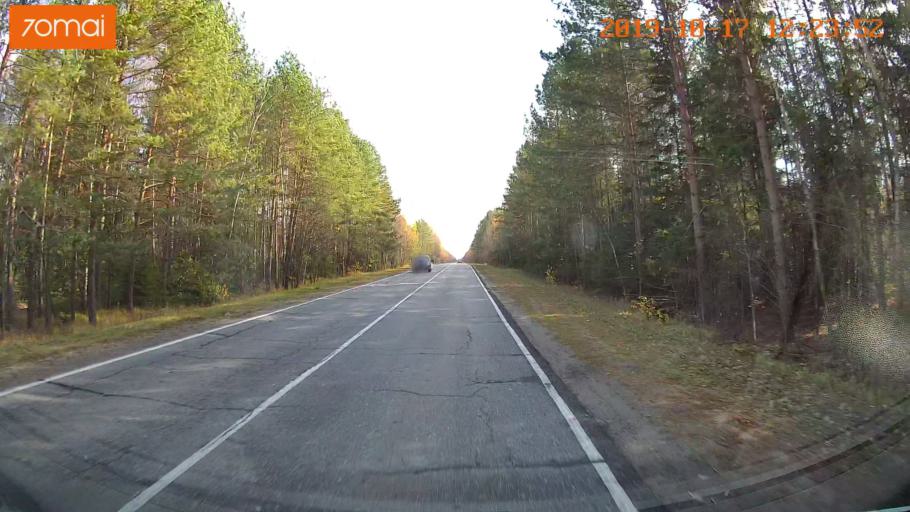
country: RU
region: Rjazan
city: Gus'-Zheleznyy
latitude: 55.0403
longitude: 41.2029
